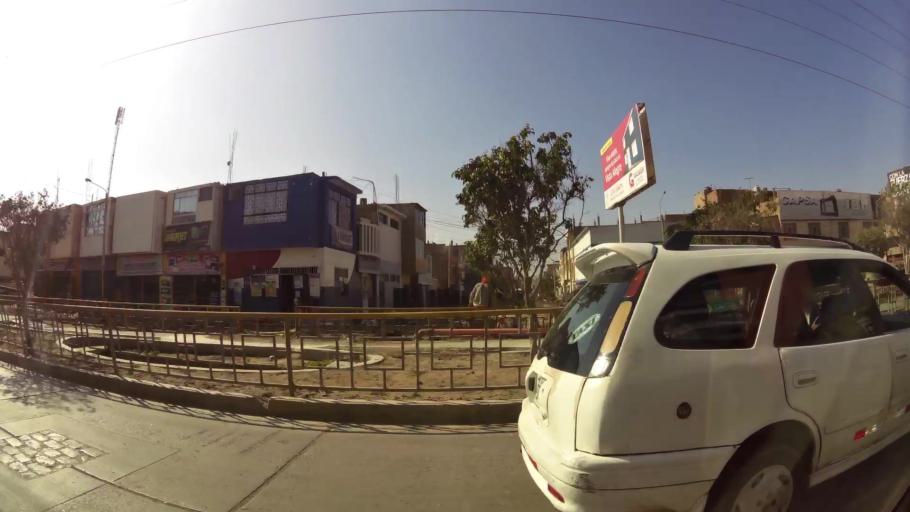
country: PE
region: Lambayeque
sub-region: Provincia de Chiclayo
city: Santa Rosa
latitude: -6.7626
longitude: -79.8404
